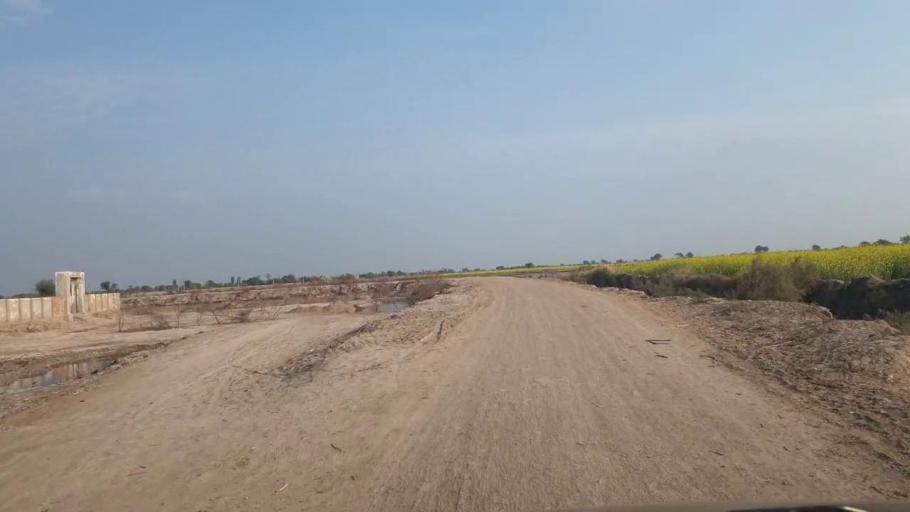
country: PK
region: Sindh
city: Shahdadpur
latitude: 25.8828
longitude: 68.7264
